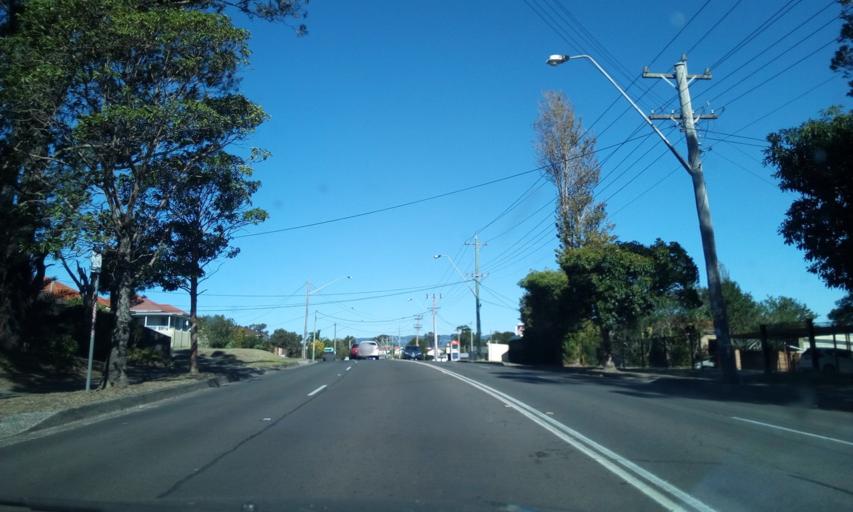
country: AU
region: New South Wales
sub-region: Wollongong
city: Dapto
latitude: -34.5041
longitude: 150.7877
